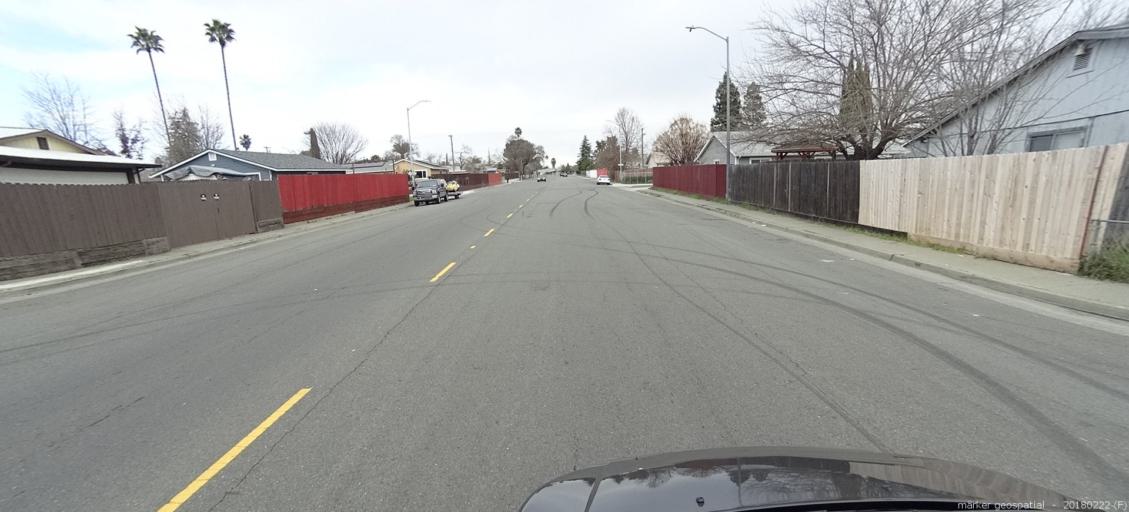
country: US
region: California
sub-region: Sacramento County
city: North Highlands
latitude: 38.7150
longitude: -121.4079
